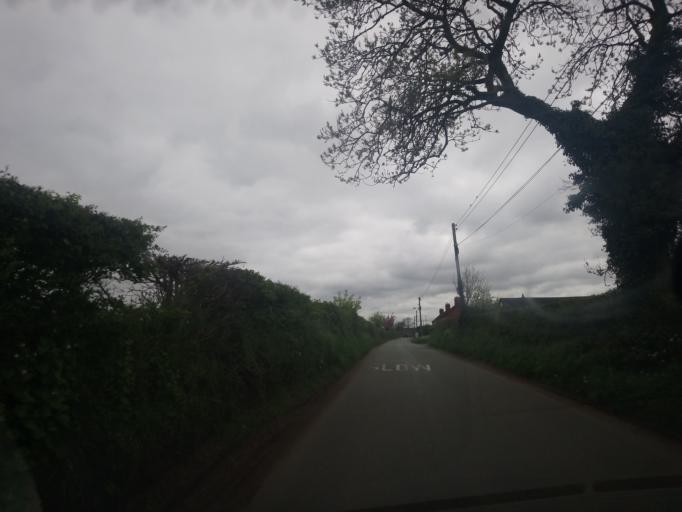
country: GB
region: England
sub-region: Shropshire
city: Stoke upon Tern
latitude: 52.8492
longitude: -2.5274
